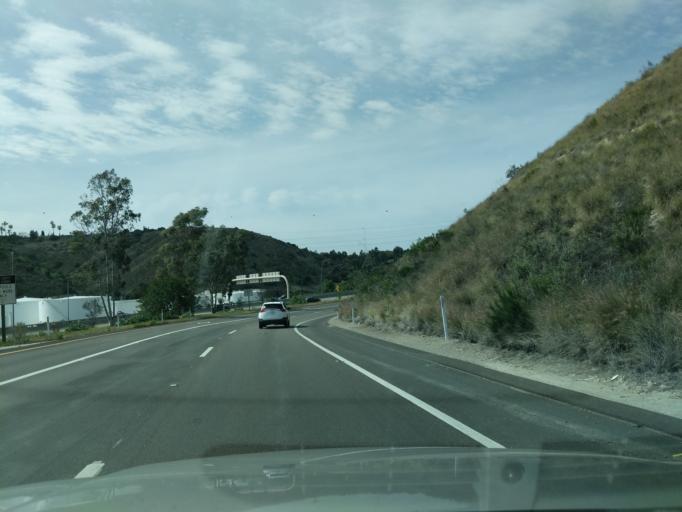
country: US
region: California
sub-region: San Diego County
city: San Diego
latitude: 32.7897
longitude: -117.1120
